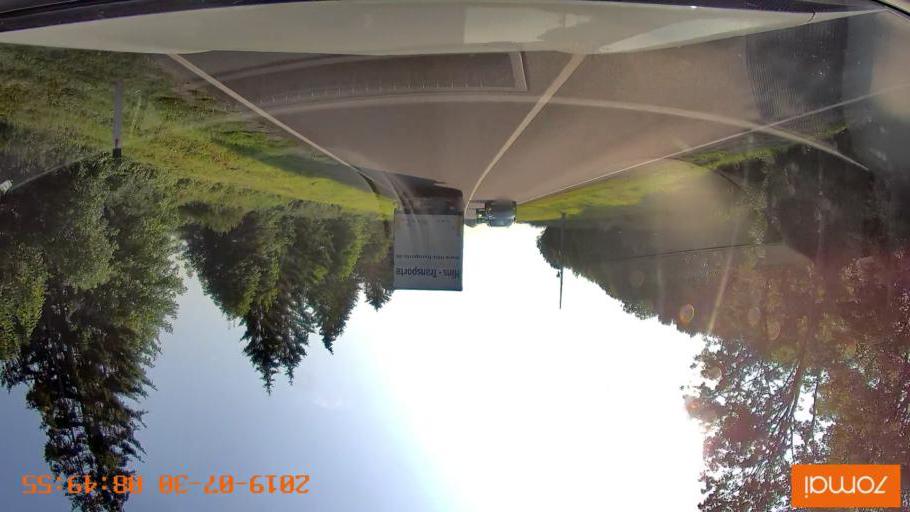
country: RU
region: Kaliningrad
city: Chernyakhovsk
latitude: 54.6103
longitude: 21.9304
